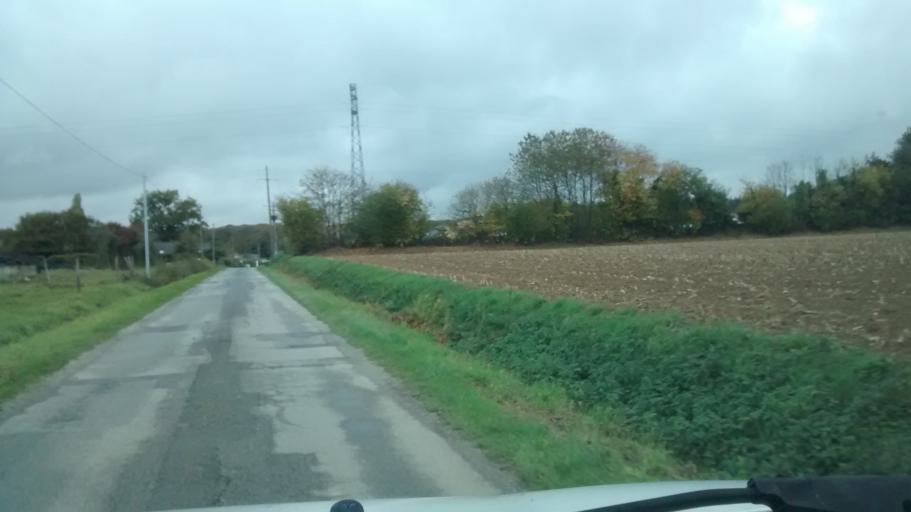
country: FR
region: Brittany
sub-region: Departement d'Ille-et-Vilaine
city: Servon-sur-Vilaine
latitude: 48.1321
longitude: -1.4431
